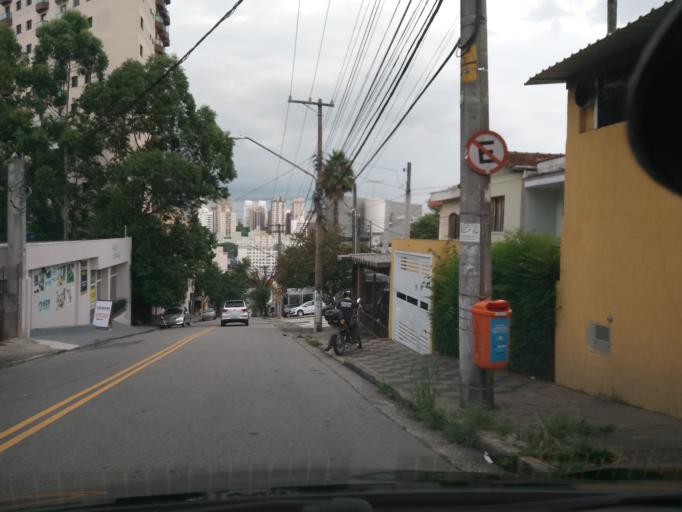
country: BR
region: Sao Paulo
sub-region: Sao Bernardo Do Campo
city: Sao Bernardo do Campo
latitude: -23.7107
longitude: -46.5562
